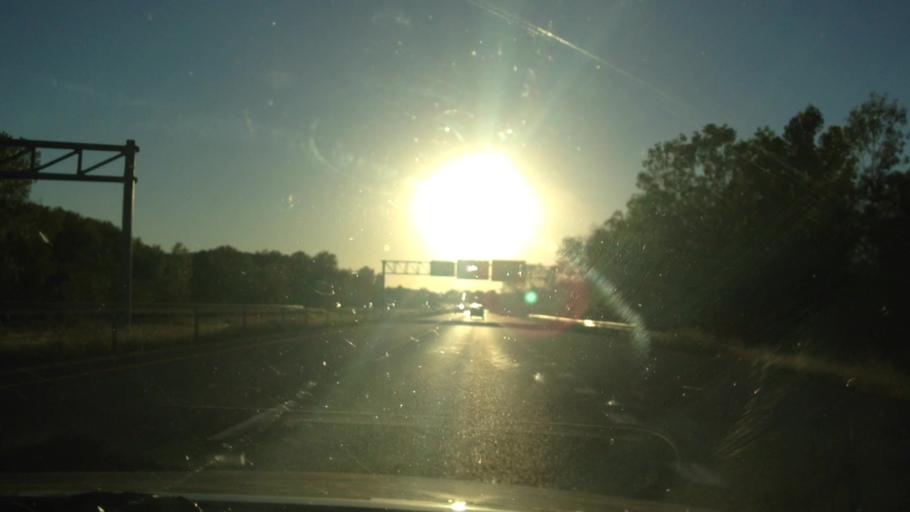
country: US
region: Missouri
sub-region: Clay County
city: Gladstone
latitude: 39.2607
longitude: -94.5795
